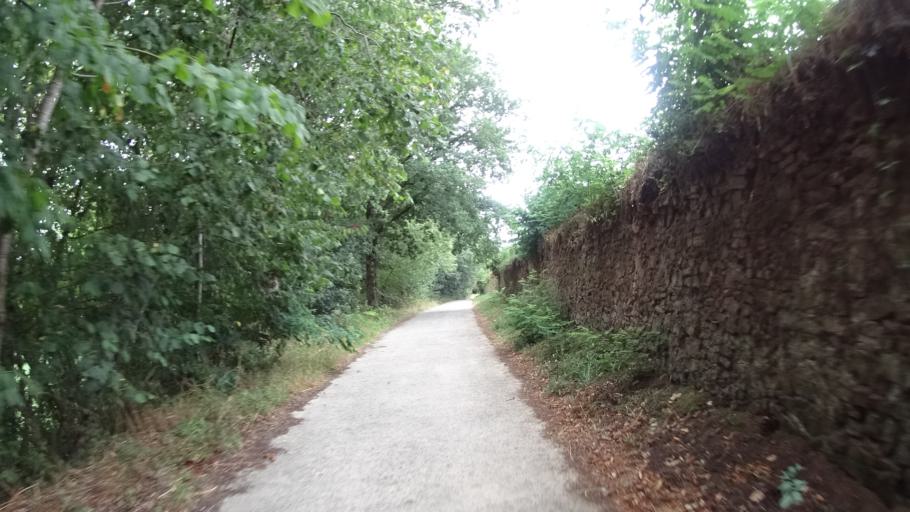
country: FR
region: Pays de la Loire
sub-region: Departement de la Loire-Atlantique
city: Le Pellerin
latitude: 47.2056
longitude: -1.7706
